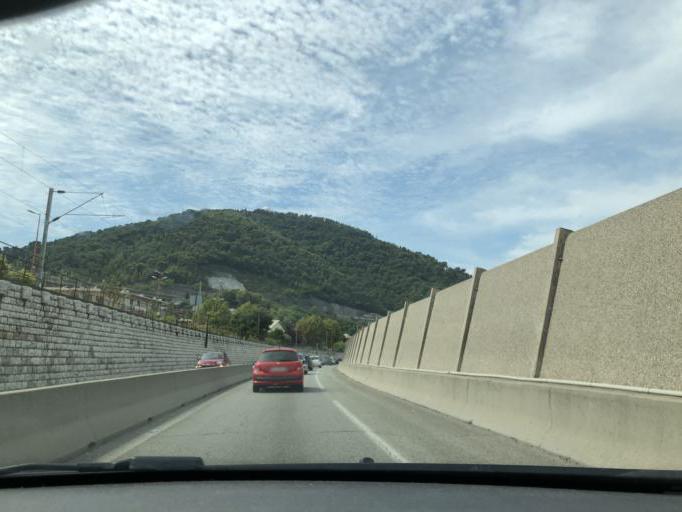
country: FR
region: Provence-Alpes-Cote d'Azur
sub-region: Departement des Alpes-Maritimes
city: La Trinite
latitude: 43.7369
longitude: 7.3079
